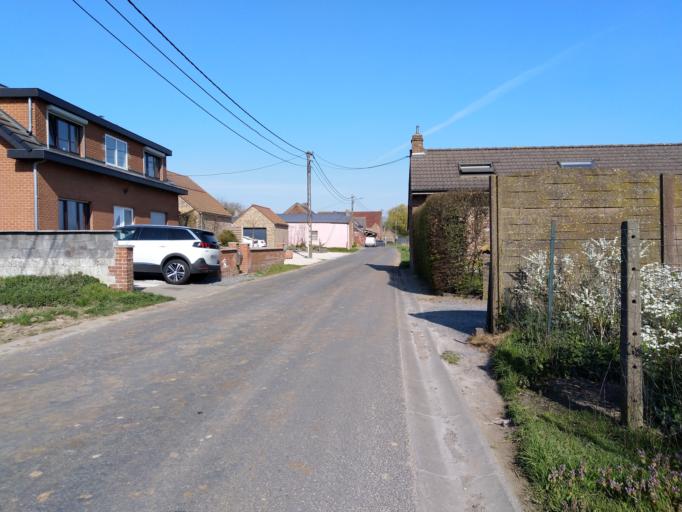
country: BE
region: Wallonia
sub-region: Province du Hainaut
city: Lens
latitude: 50.5527
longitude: 3.8833
